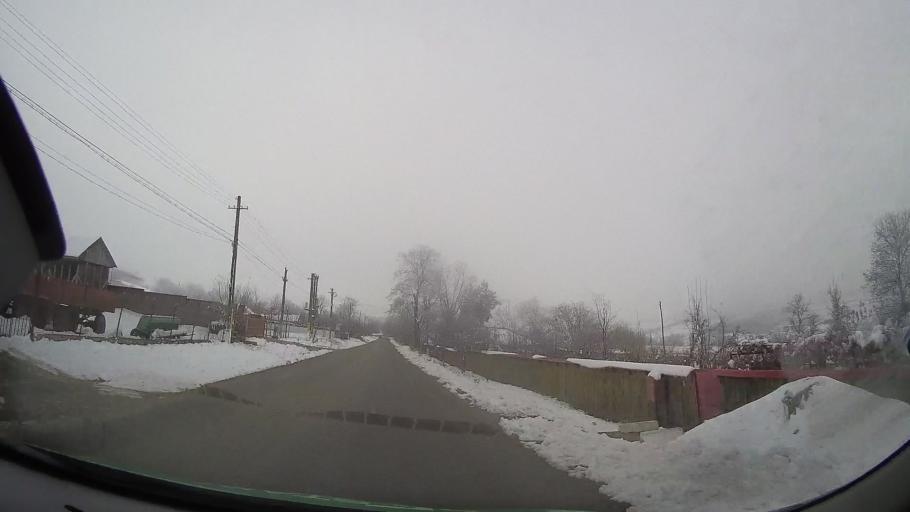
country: RO
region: Bacau
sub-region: Comuna Oncesti
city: Oncesti
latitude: 46.4438
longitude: 27.2656
